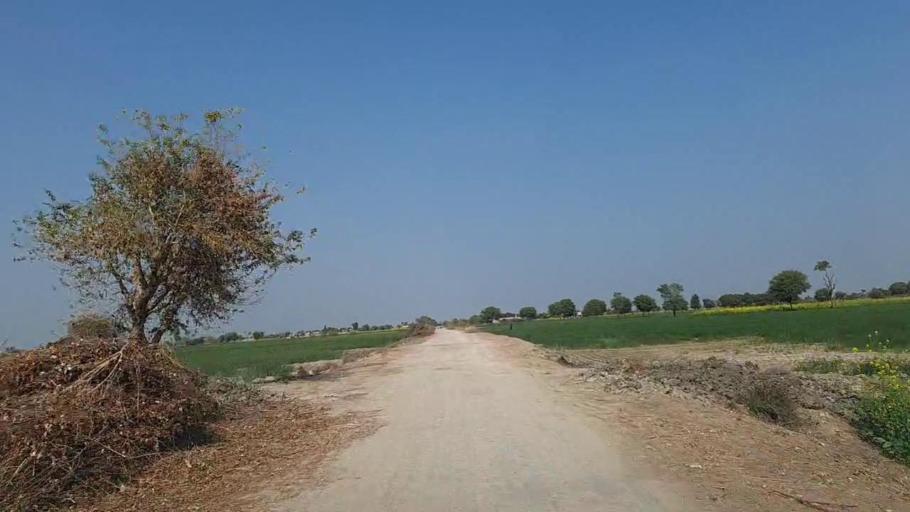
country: PK
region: Sindh
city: Nawabshah
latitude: 26.2732
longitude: 68.5135
